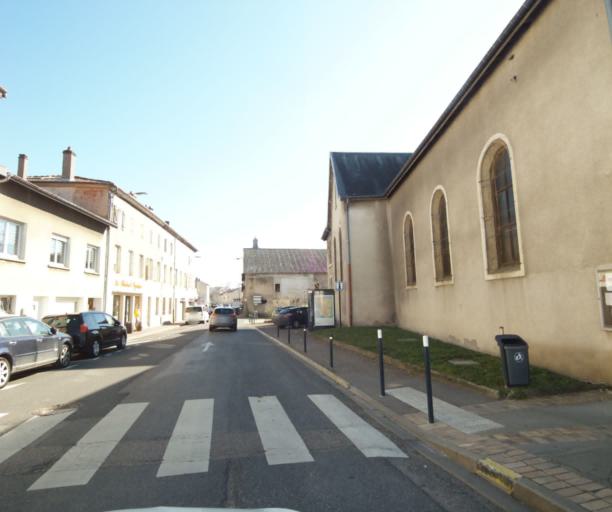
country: FR
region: Lorraine
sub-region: Departement de Meurthe-et-Moselle
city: Tomblaine
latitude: 48.6864
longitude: 6.2109
